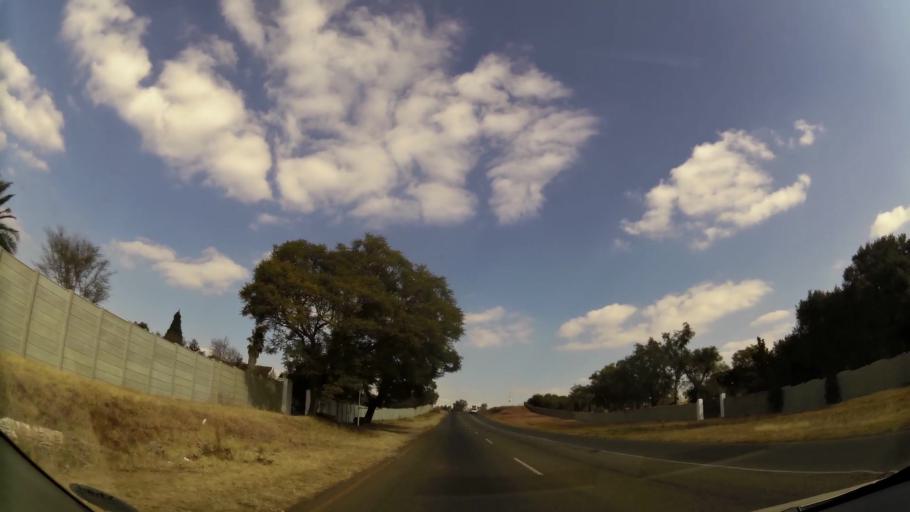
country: ZA
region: Gauteng
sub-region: West Rand District Municipality
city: Krugersdorp
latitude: -26.0491
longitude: 27.7542
